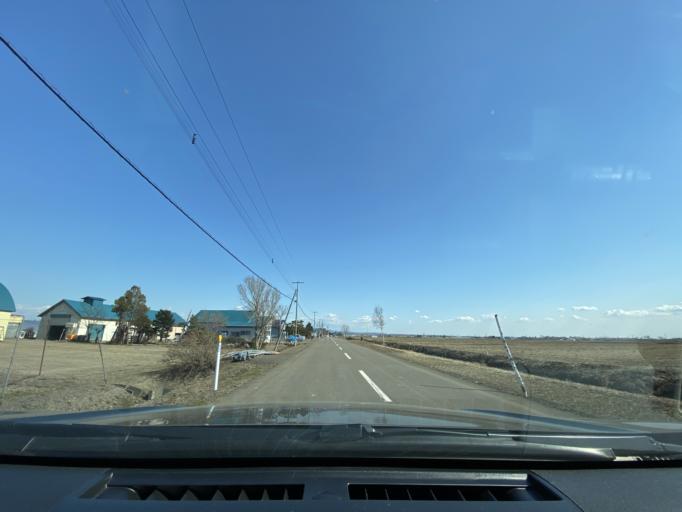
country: JP
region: Hokkaido
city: Iwamizawa
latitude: 43.2919
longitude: 141.6829
